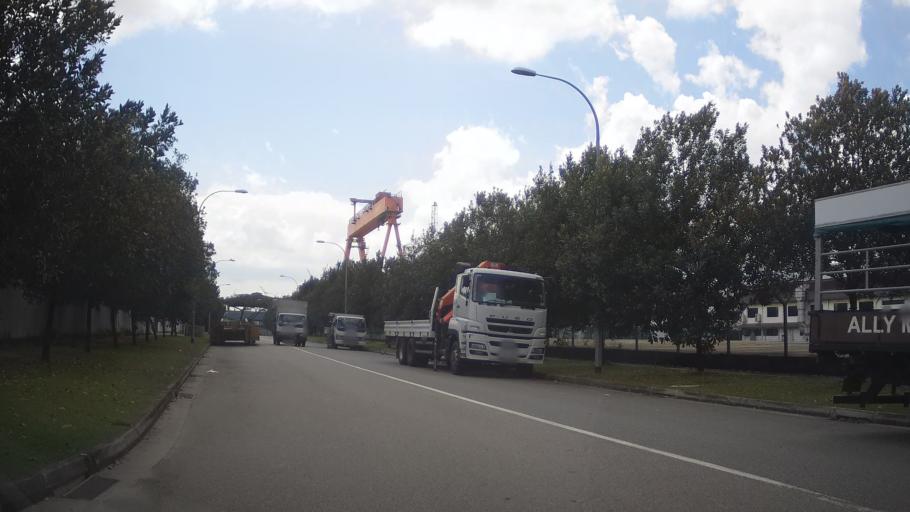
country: MY
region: Johor
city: Johor Bahru
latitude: 1.3094
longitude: 103.6484
